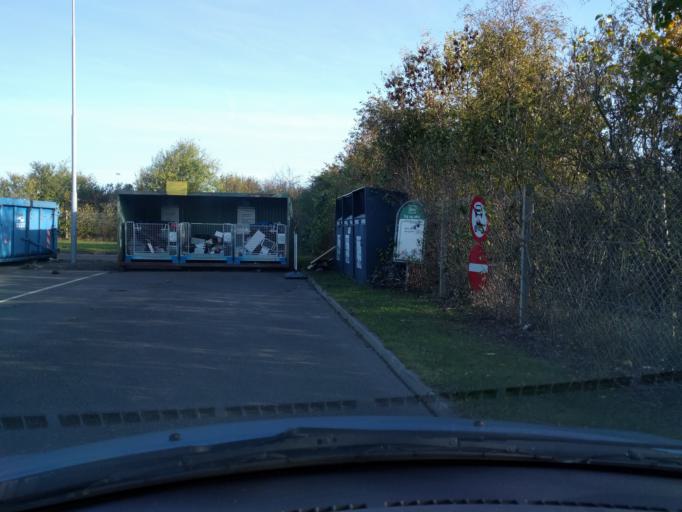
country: DK
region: South Denmark
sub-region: Kerteminde Kommune
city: Munkebo
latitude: 55.4572
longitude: 10.5414
